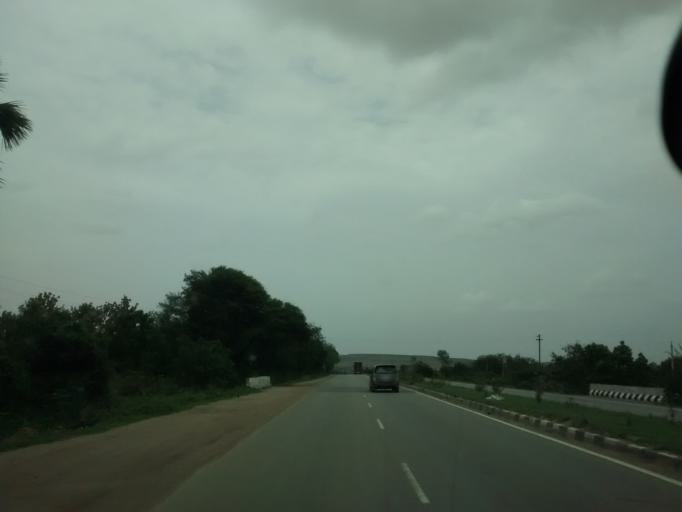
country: IN
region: Andhra Pradesh
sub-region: Kurnool
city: Ramapuram
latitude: 15.2562
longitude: 77.7561
